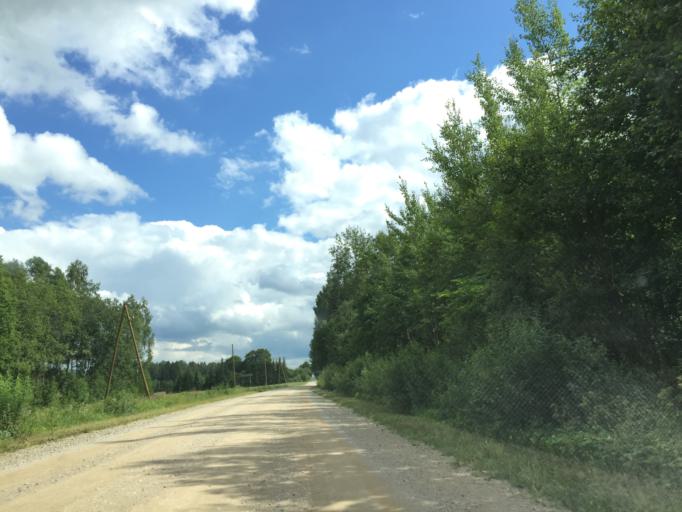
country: LV
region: Malpils
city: Malpils
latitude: 56.8746
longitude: 25.0025
